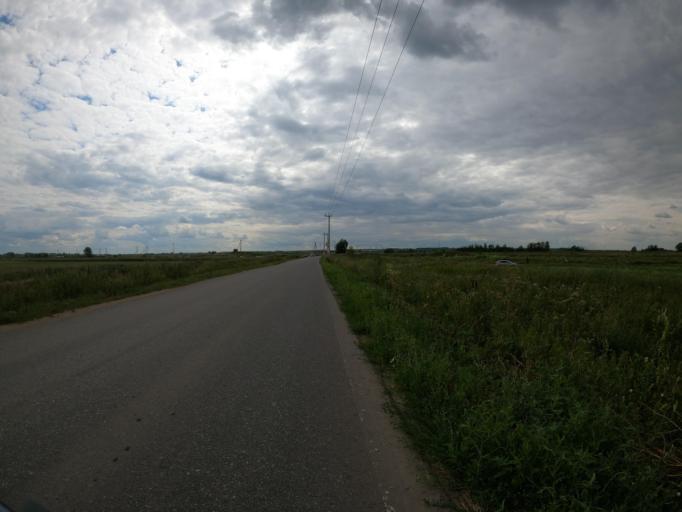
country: RU
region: Moskovskaya
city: Ramenskoye
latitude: 55.5082
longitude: 38.2234
